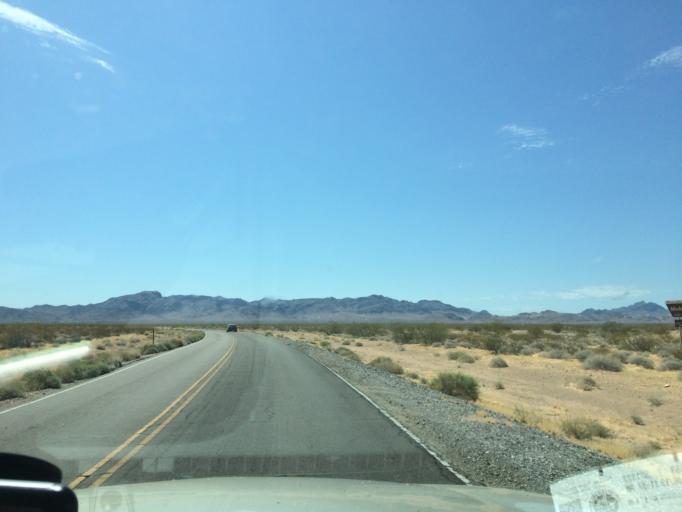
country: US
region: Nevada
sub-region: Clark County
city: Moapa Town
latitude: 36.4604
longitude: -114.7354
